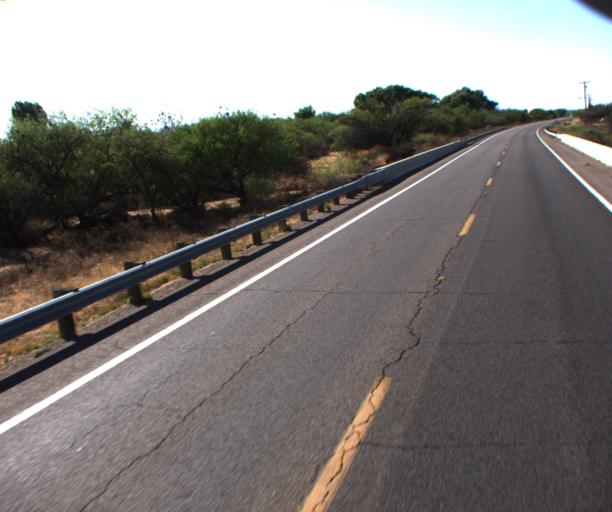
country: US
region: Arizona
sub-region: Cochise County
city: Saint David
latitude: 31.8754
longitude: -110.2102
